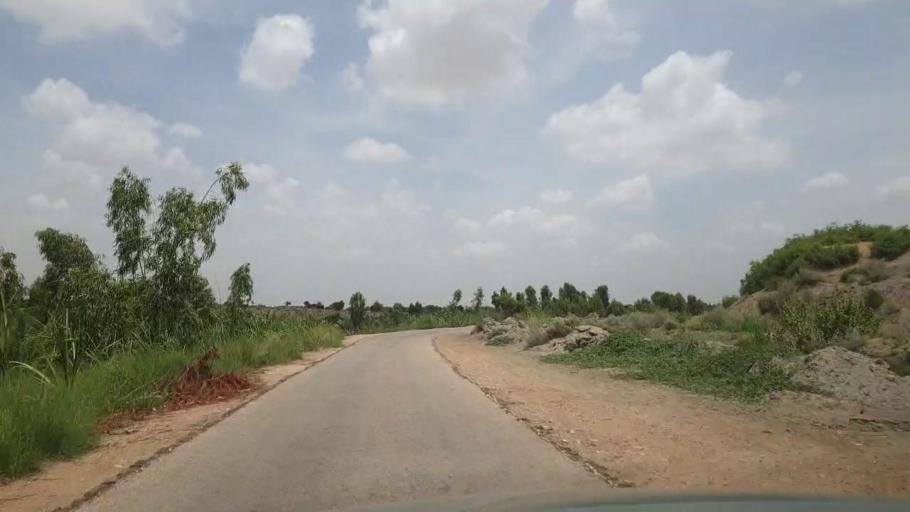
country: PK
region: Sindh
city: Kot Diji
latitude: 27.1988
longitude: 69.0697
